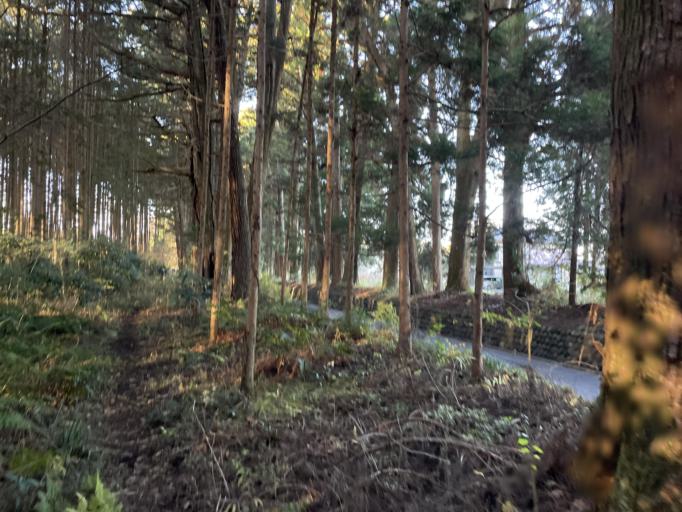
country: JP
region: Tochigi
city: Imaichi
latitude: 36.6515
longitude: 139.7220
